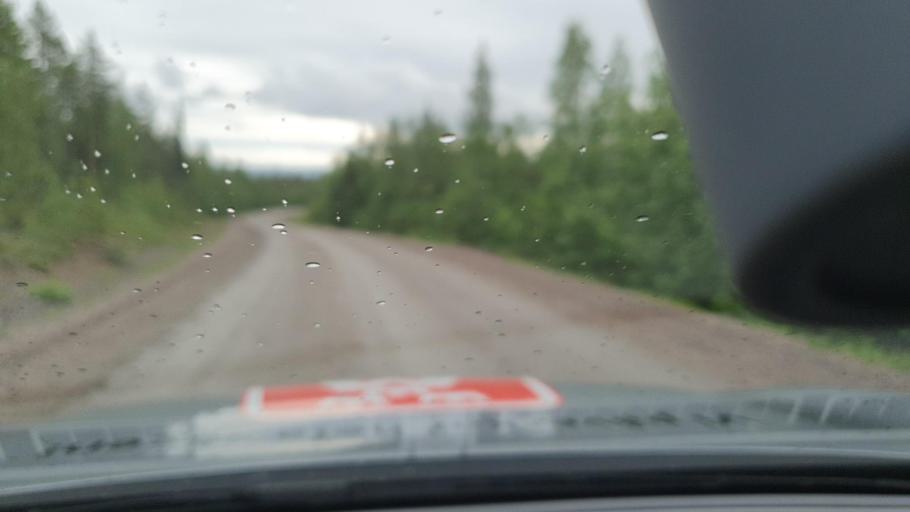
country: SE
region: Norrbotten
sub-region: Overtornea Kommun
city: OEvertornea
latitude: 66.4391
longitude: 23.5019
